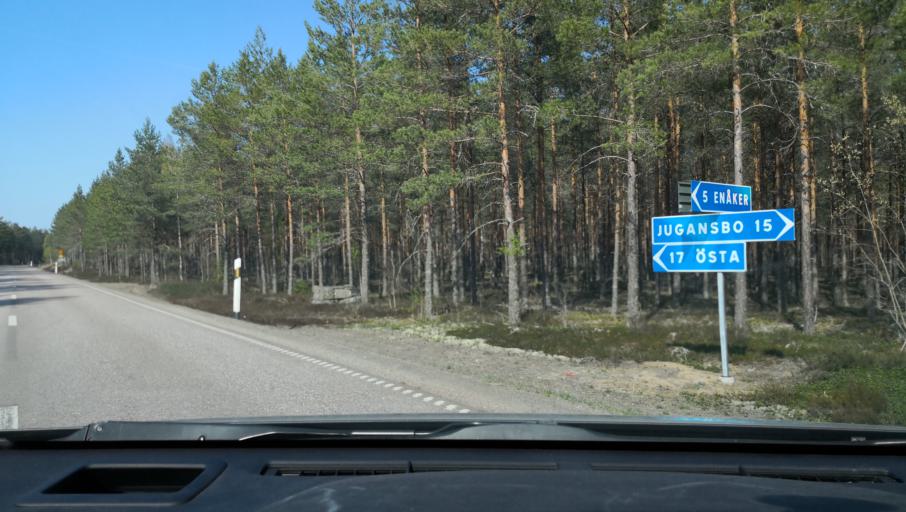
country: SE
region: Uppsala
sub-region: Heby Kommun
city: Heby
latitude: 60.0515
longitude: 16.8663
